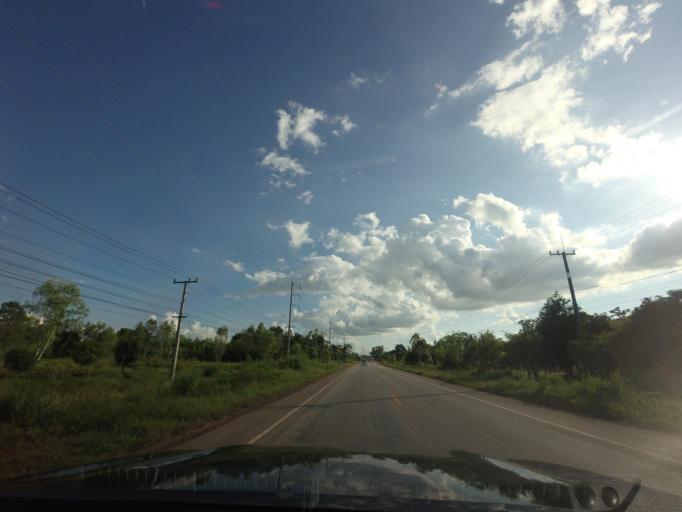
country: TH
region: Changwat Udon Thani
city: Thung Fon
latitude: 17.4934
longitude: 103.1999
